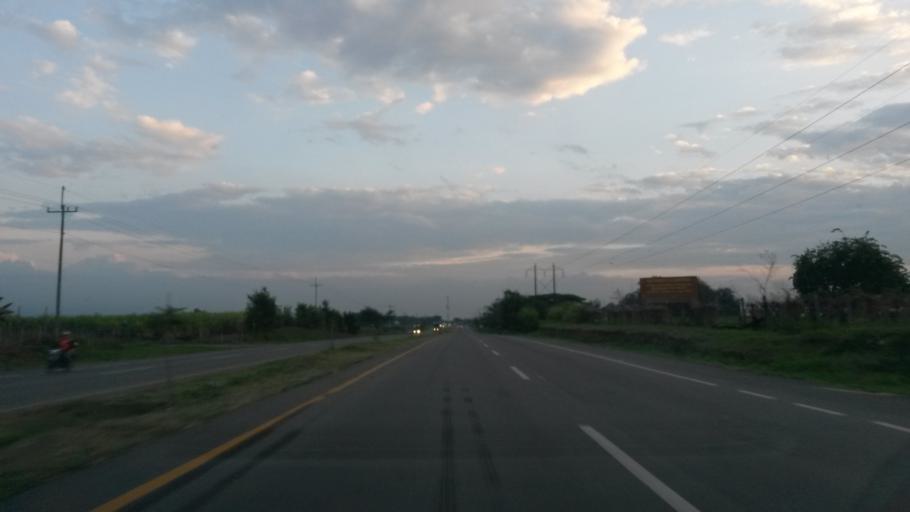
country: CO
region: Cauca
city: Santander de Quilichao
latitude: 3.0648
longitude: -76.4748
